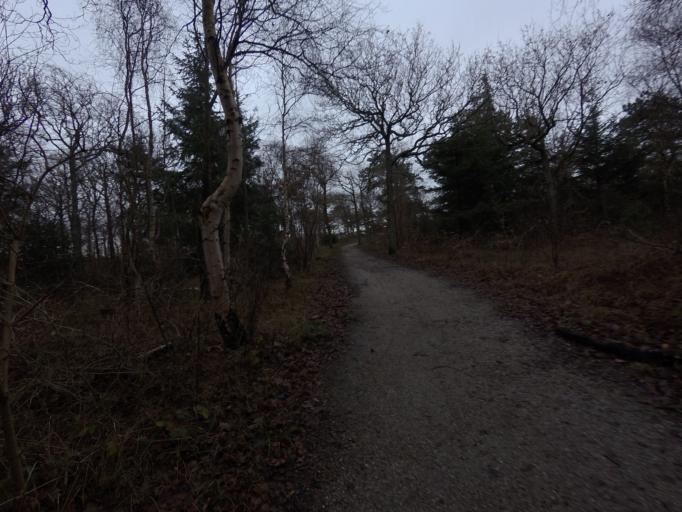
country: NL
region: North Holland
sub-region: Gemeente Texel
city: Den Burg
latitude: 53.0819
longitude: 4.7490
